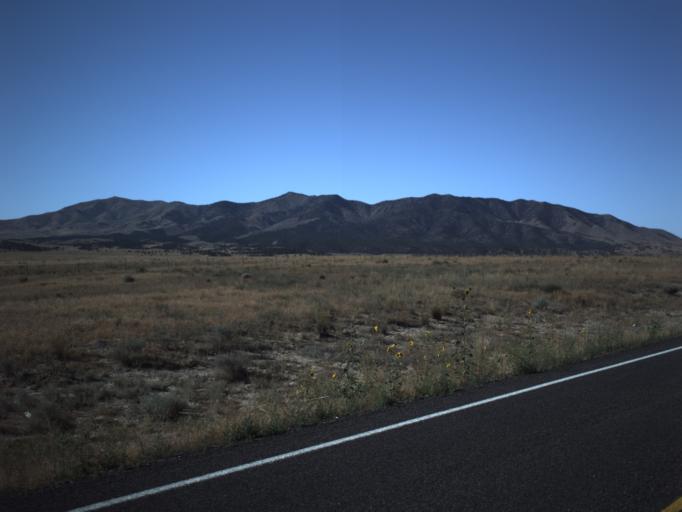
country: US
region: Utah
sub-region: Juab County
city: Mona
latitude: 39.7015
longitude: -112.2187
